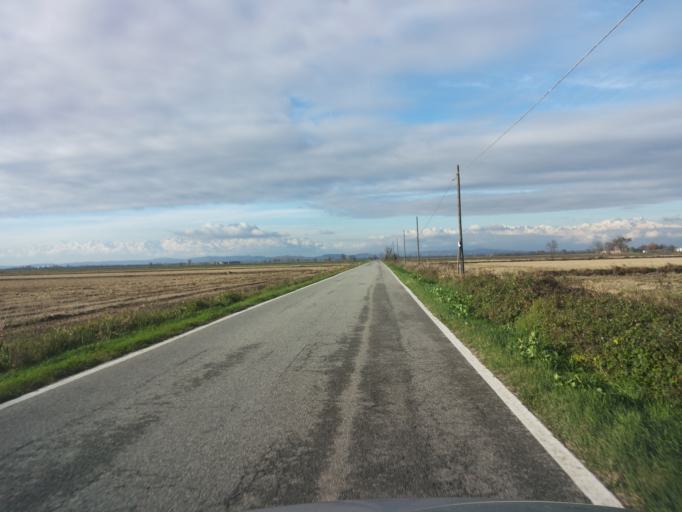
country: IT
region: Piedmont
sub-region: Provincia di Vercelli
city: Crova
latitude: 45.3020
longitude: 8.2127
